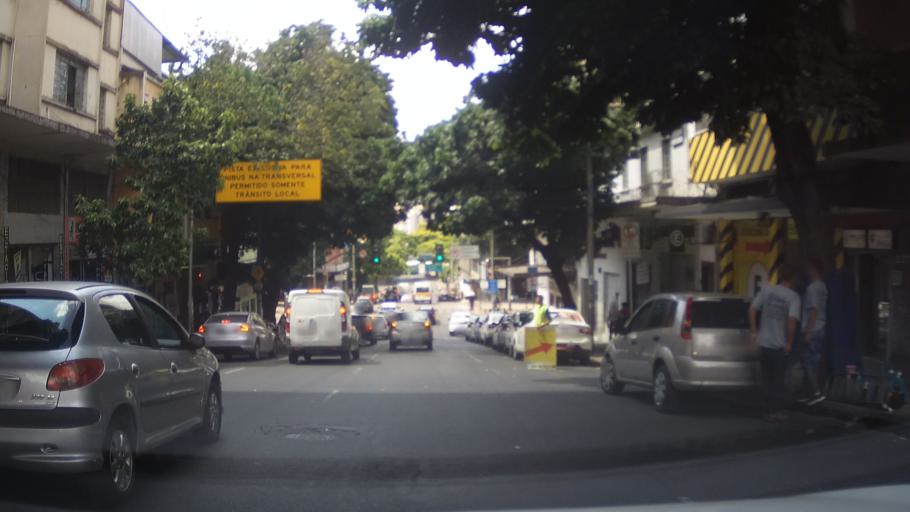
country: BR
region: Minas Gerais
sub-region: Belo Horizonte
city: Belo Horizonte
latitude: -19.9169
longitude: -43.9368
